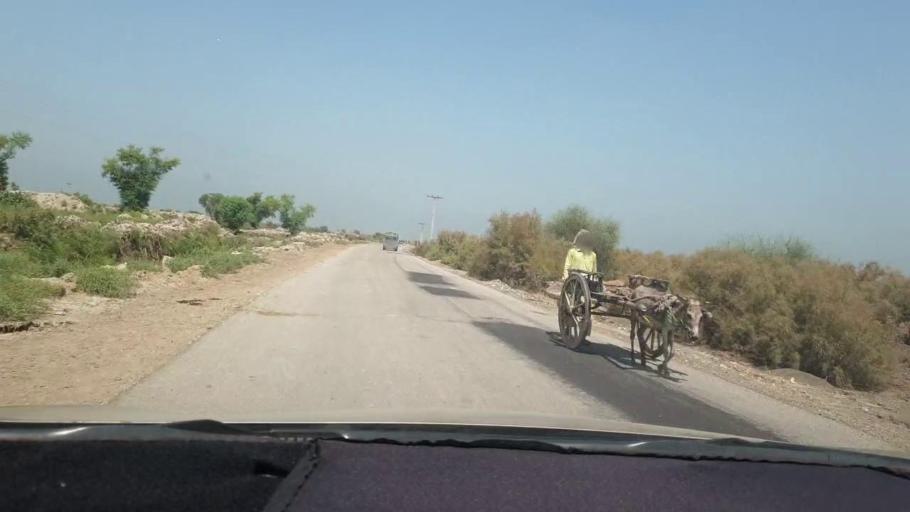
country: PK
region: Sindh
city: Miro Khan
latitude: 27.8225
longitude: 68.0218
